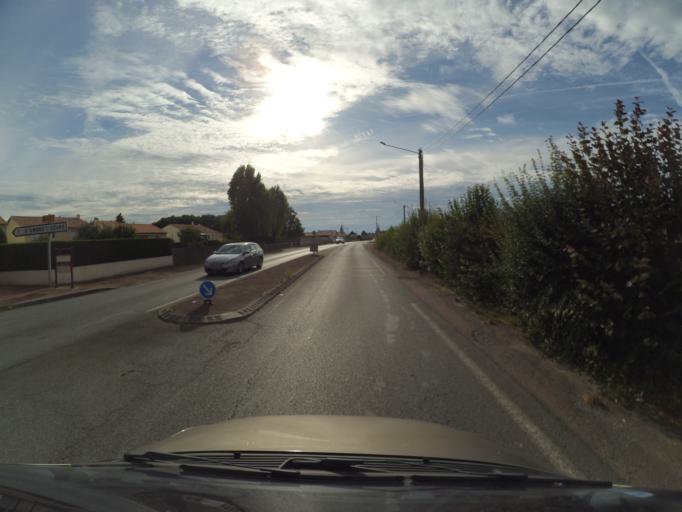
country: FR
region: Poitou-Charentes
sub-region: Departement des Deux-Sevres
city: Saint-Amand-sur-Sevre
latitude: 46.9281
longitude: -0.8089
